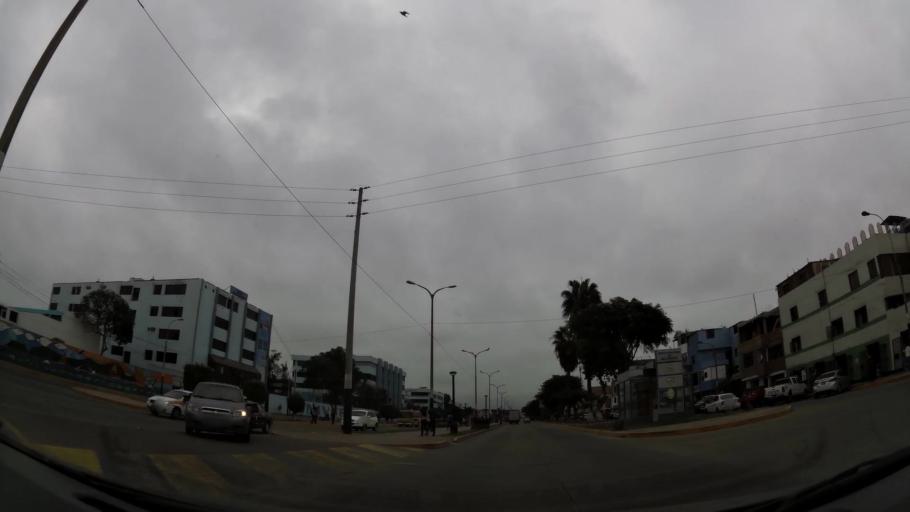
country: PE
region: Callao
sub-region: Callao
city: Callao
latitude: -12.0636
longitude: -77.1179
